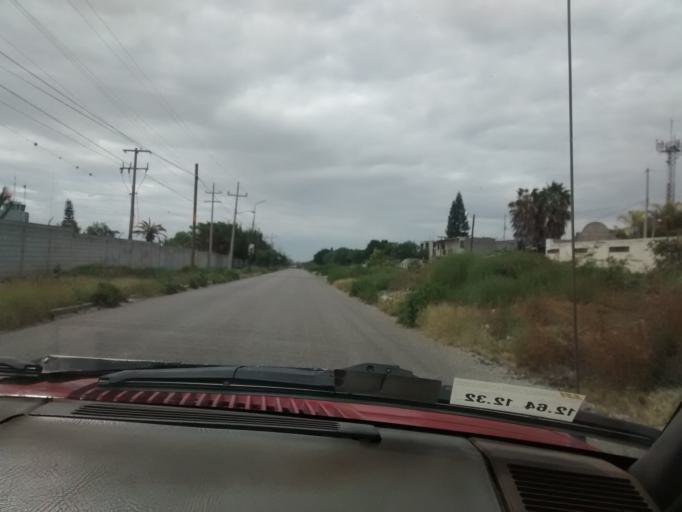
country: MX
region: Puebla
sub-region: Santiago Miahuatlan
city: San Jose Monte Chiquito
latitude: 18.4930
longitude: -97.4200
